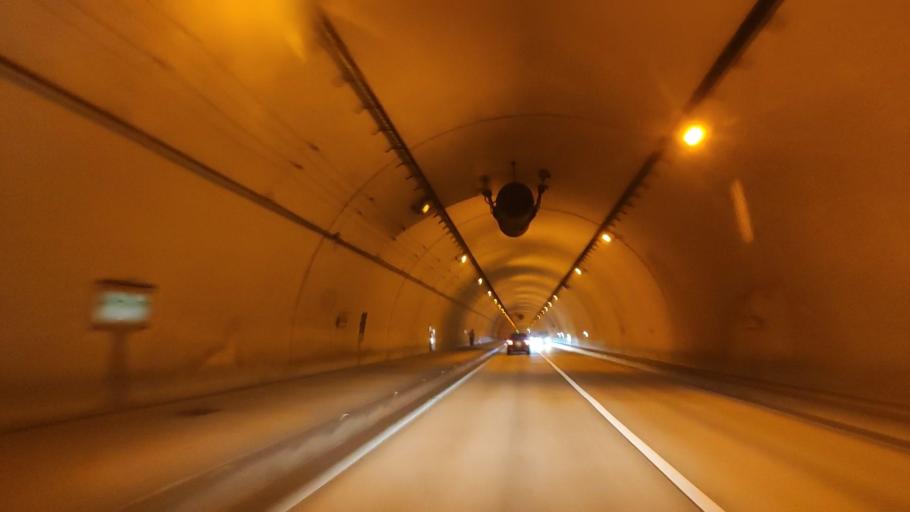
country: JP
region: Ehime
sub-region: Shikoku-chuo Shi
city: Matsuyama
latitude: 33.8778
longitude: 132.7132
